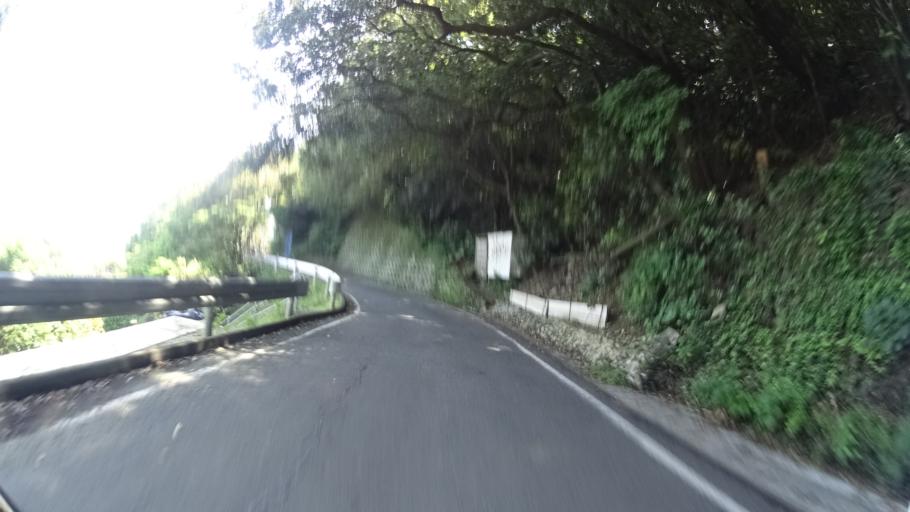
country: JP
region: Oita
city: Tsukumiura
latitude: 33.3475
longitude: 132.0231
